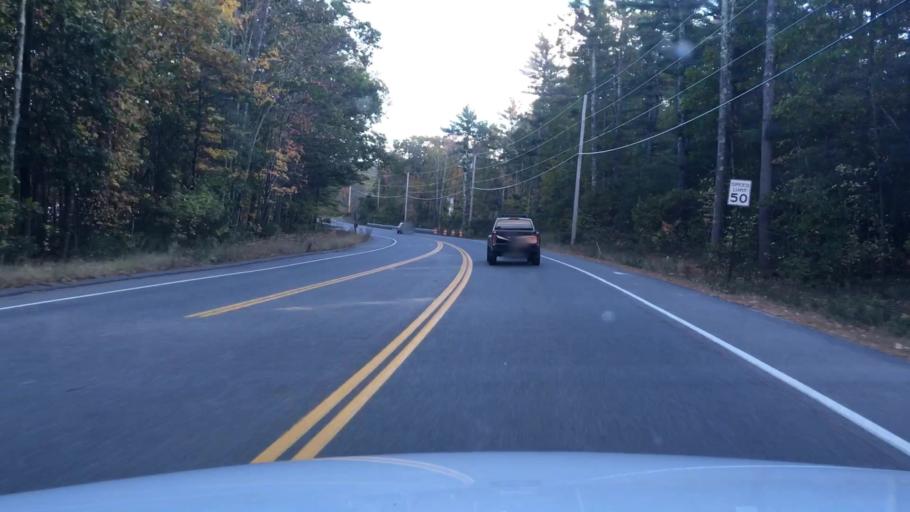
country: US
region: Maine
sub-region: York County
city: Wells Beach Station
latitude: 43.3458
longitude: -70.6445
